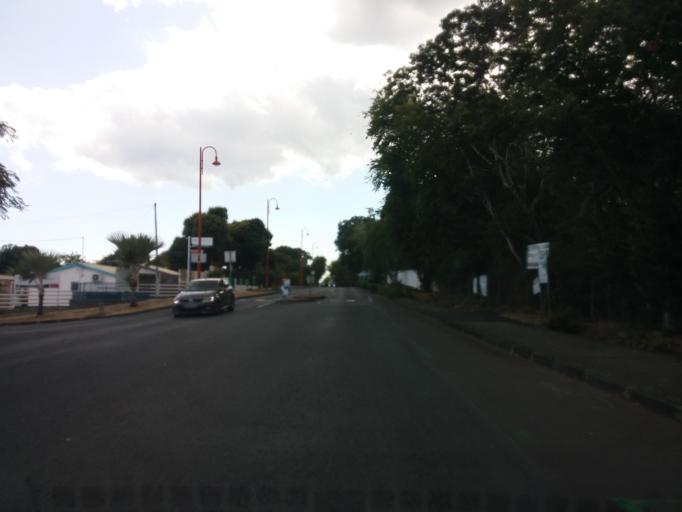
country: RE
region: Reunion
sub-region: Reunion
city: La Possession
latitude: -20.9363
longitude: 55.3333
